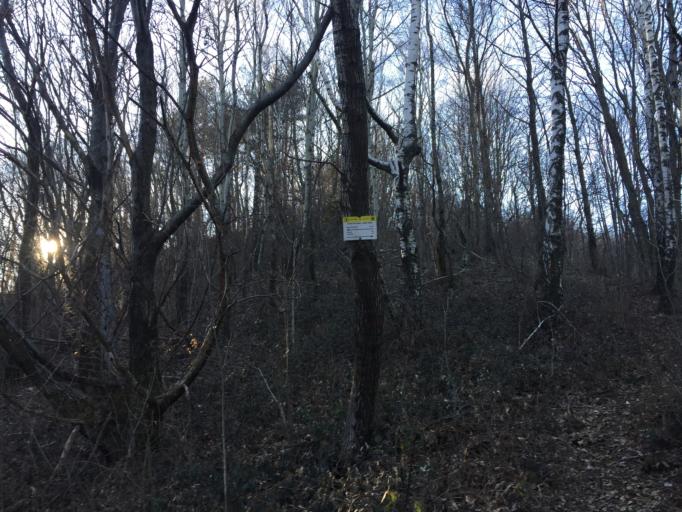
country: IT
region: Friuli Venezia Giulia
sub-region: Provincia di Udine
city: Taipana
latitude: 46.2342
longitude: 13.3227
